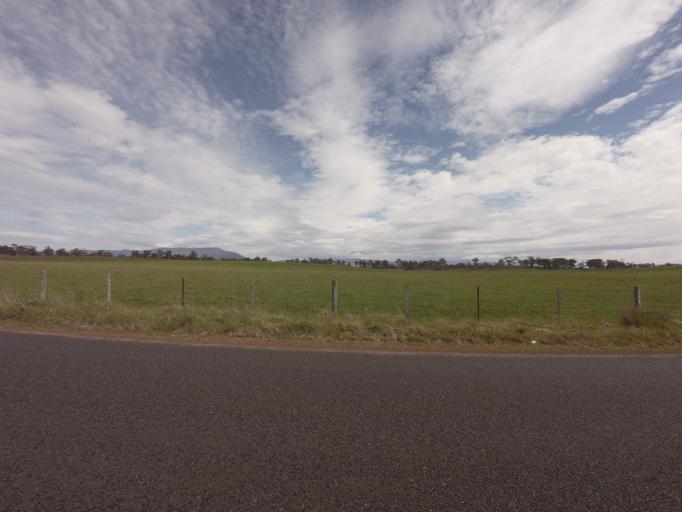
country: AU
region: Tasmania
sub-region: Northern Midlands
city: Evandale
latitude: -41.7948
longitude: 147.2521
